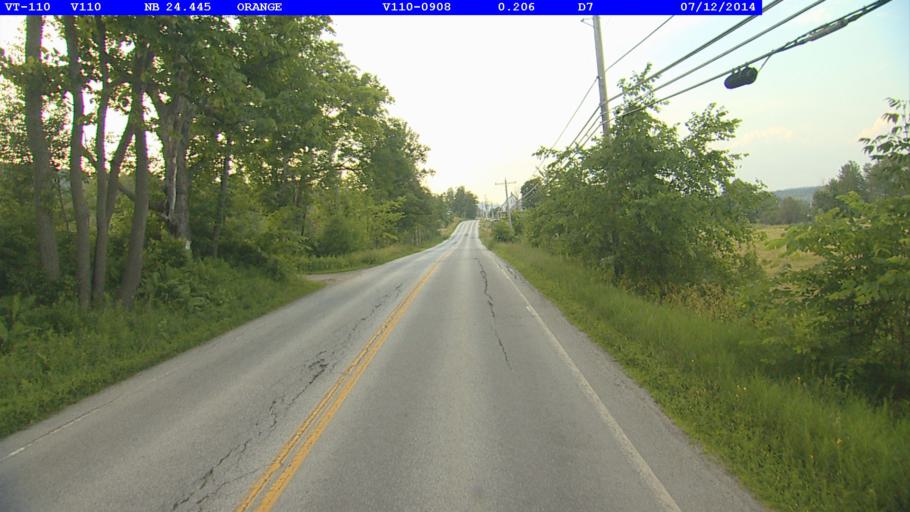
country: US
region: Vermont
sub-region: Washington County
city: South Barre
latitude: 44.1272
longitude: -72.4300
